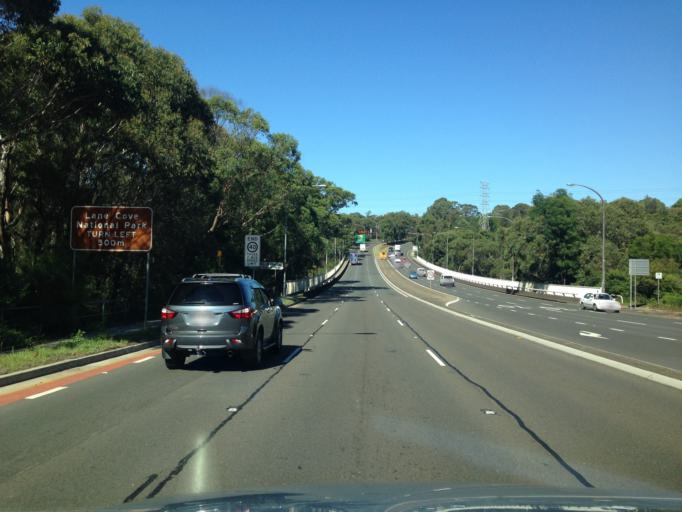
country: AU
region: New South Wales
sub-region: Ryde
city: Macquarie Park
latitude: -33.7742
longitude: 151.1354
